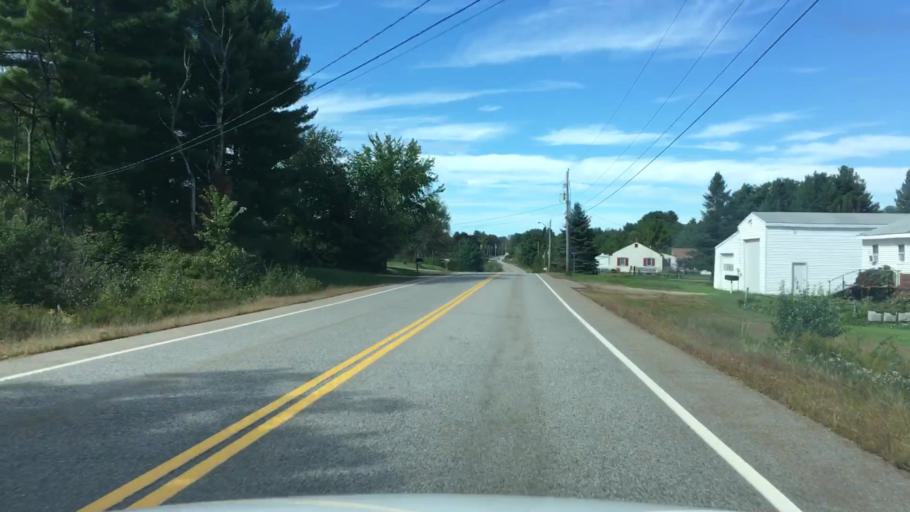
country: US
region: Maine
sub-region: Cumberland County
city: Westbrook
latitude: 43.6635
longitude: -70.4050
